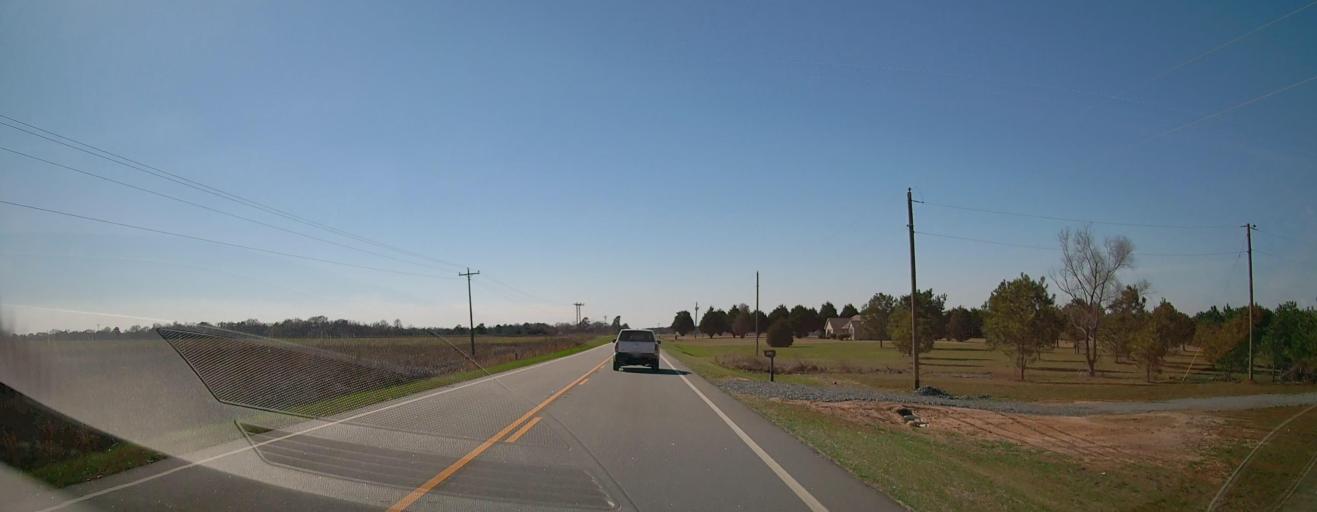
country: US
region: Georgia
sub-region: Dooly County
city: Unadilla
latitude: 32.3378
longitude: -83.8333
